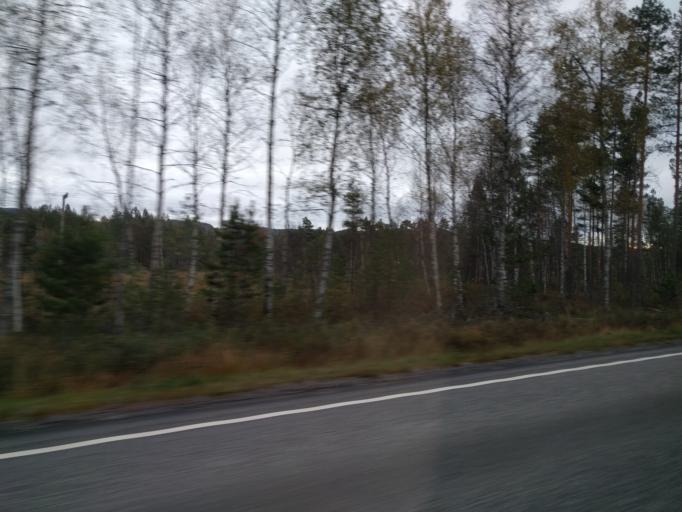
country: NO
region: Aust-Agder
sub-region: Evje og Hornnes
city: Evje
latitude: 58.5286
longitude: 7.7795
